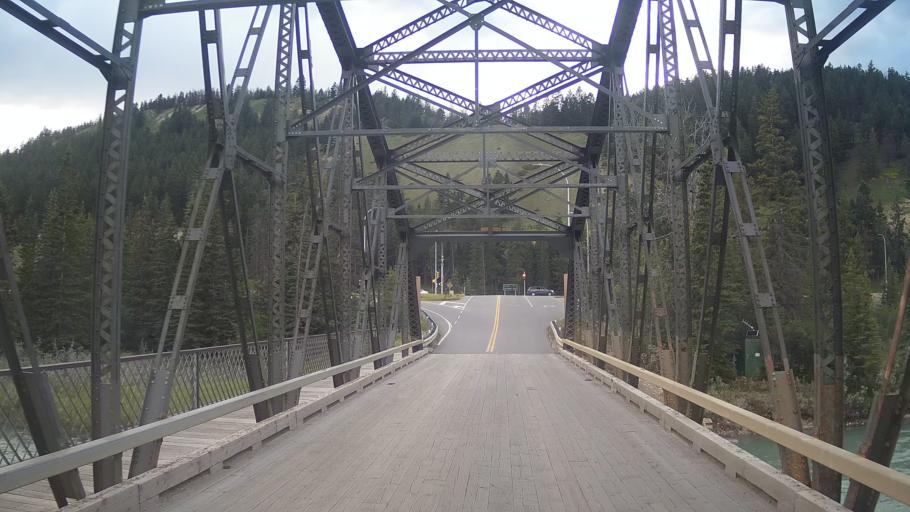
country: CA
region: Alberta
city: Jasper Park Lodge
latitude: 52.9095
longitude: -118.0579
